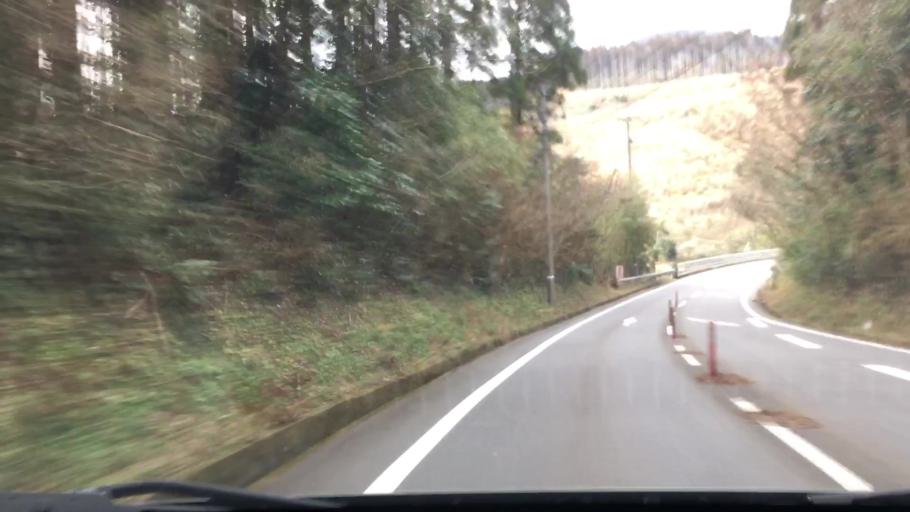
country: JP
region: Miyazaki
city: Nichinan
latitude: 31.7071
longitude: 131.3276
